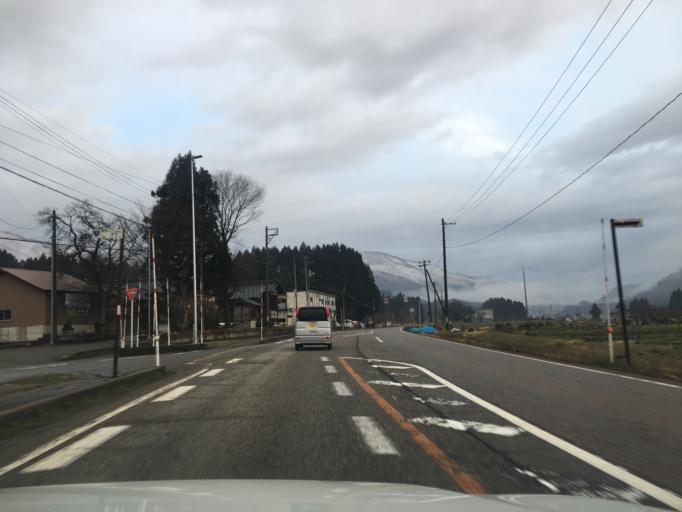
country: JP
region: Niigata
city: Murakami
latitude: 38.3356
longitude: 139.5523
